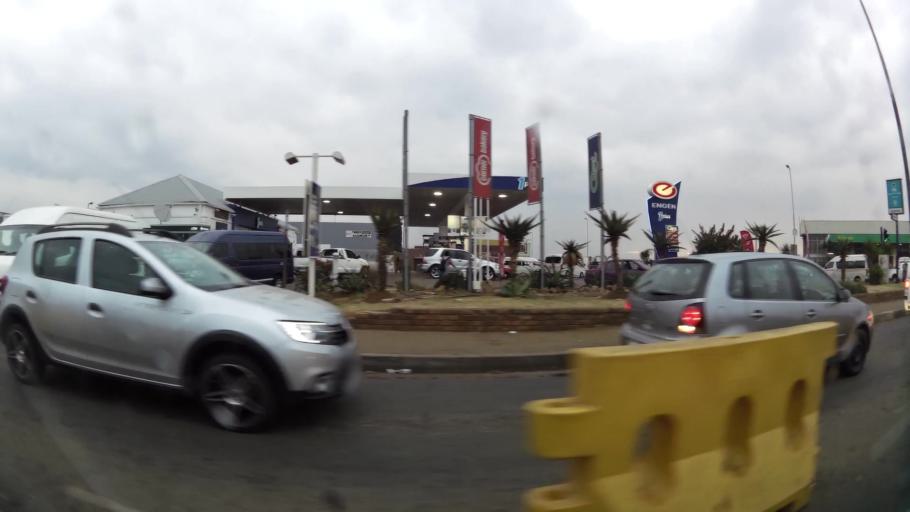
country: ZA
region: Gauteng
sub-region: City of Johannesburg Metropolitan Municipality
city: Soweto
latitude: -26.2487
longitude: 27.8540
